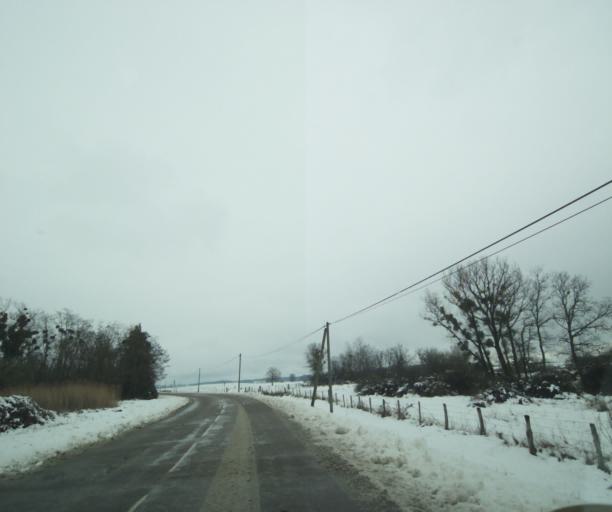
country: FR
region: Champagne-Ardenne
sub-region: Departement de la Haute-Marne
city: Montier-en-Der
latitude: 48.4531
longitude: 4.7743
